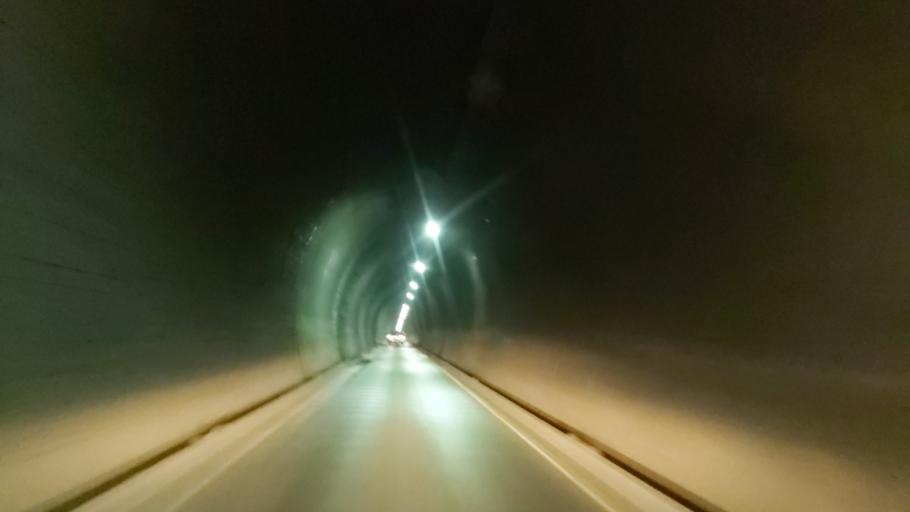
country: CL
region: Araucania
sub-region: Provincia de Cautin
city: Vilcun
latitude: -38.5375
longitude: -71.5076
